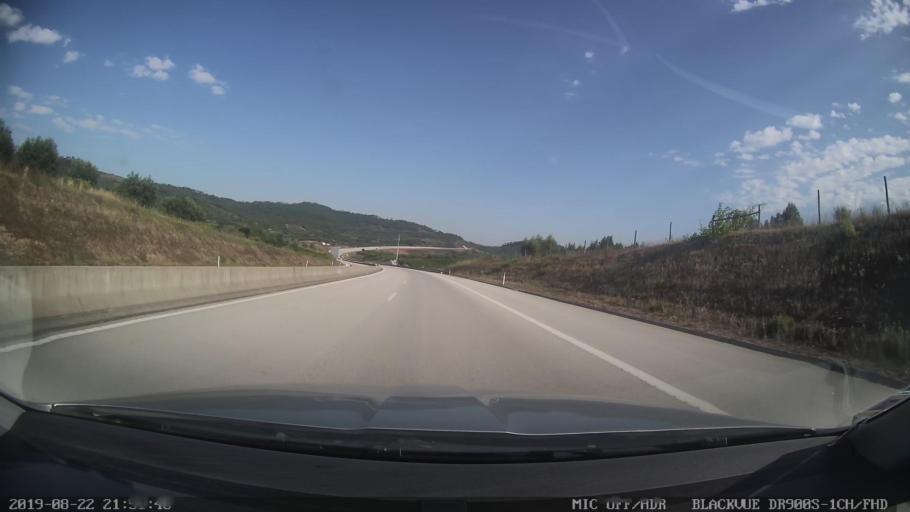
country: PT
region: Coimbra
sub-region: Miranda do Corvo
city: Miranda do Corvo
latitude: 40.0876
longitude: -8.3858
